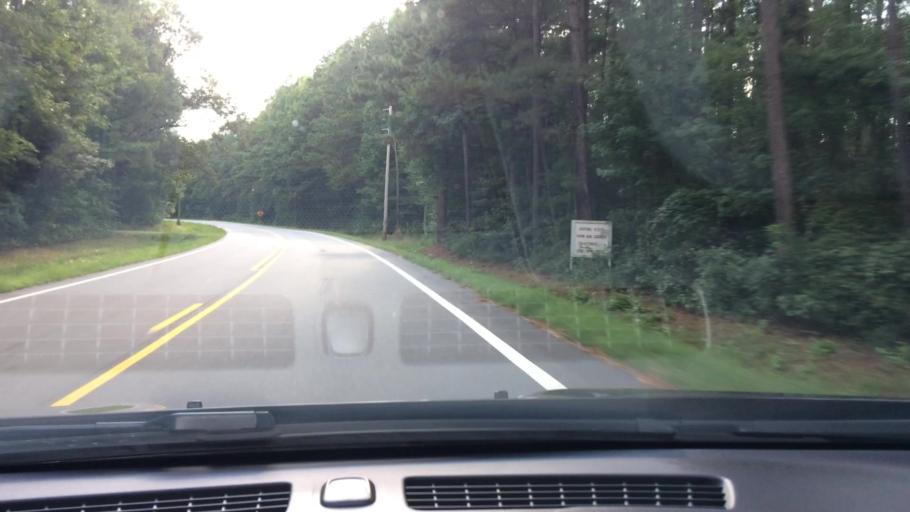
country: US
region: North Carolina
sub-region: Craven County
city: Vanceboro
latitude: 35.4195
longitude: -77.2516
